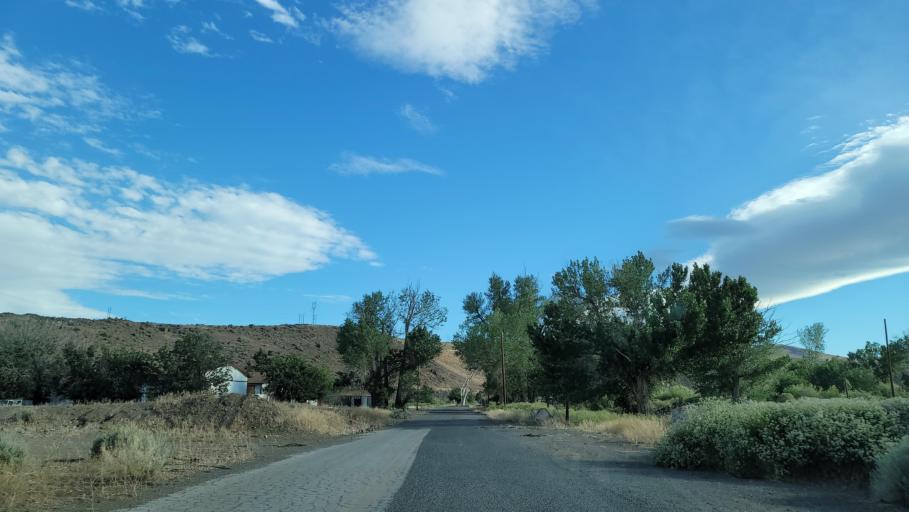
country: US
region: Nevada
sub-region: Washoe County
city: Sparks
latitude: 39.5165
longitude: -119.6181
